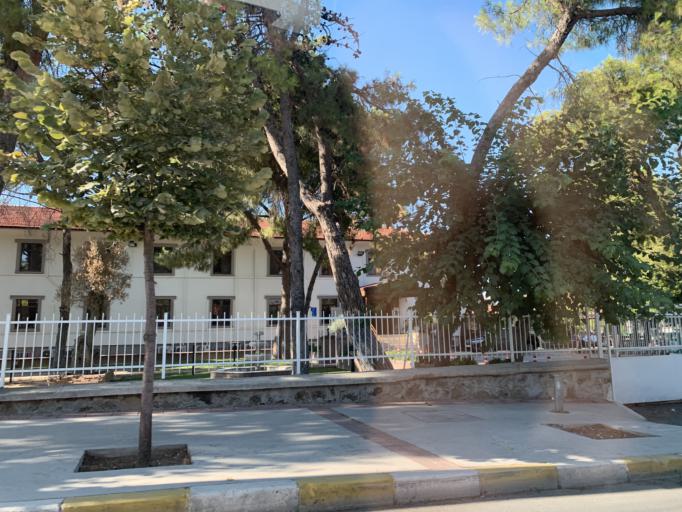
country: TR
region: Izmir
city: Urla
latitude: 38.3215
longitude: 26.7618
